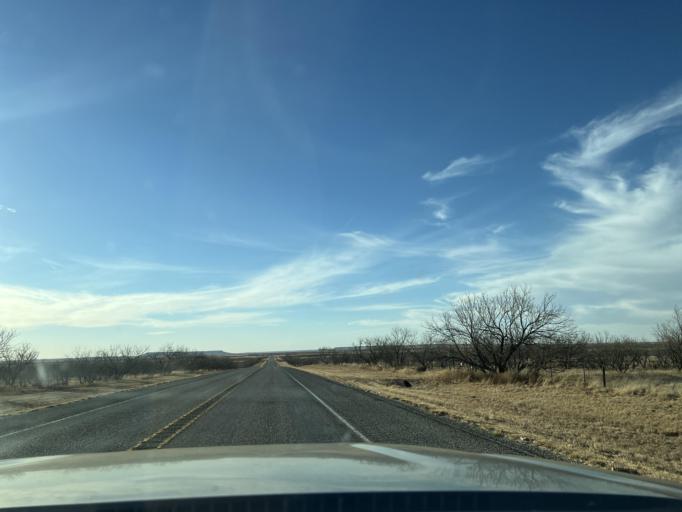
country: US
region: Texas
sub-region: Borden County
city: Gail
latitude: 32.7691
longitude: -101.3182
